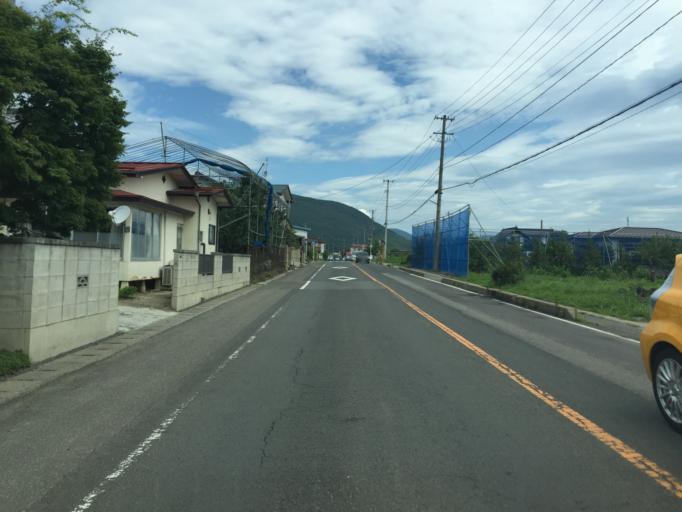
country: JP
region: Fukushima
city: Fukushima-shi
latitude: 37.7908
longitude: 140.4000
